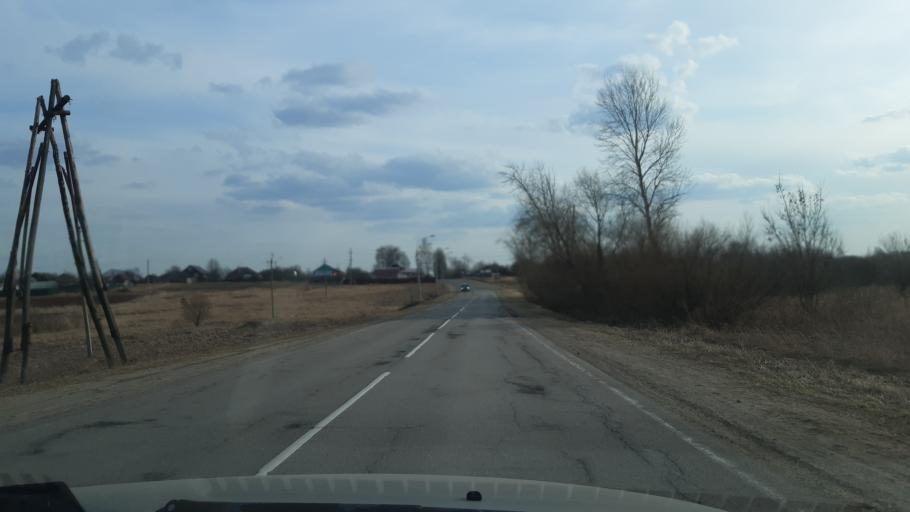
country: RU
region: Vladimir
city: Nikologory
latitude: 56.1542
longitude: 41.9958
